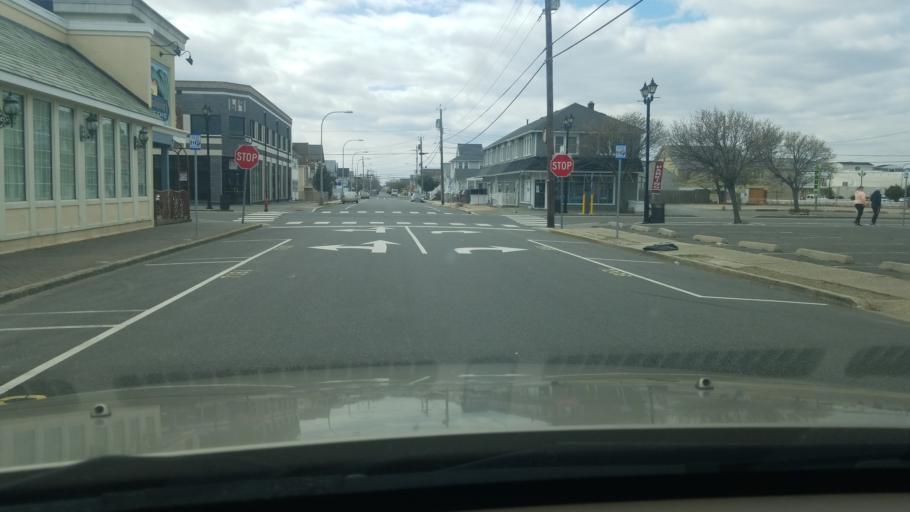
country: US
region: New Jersey
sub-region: Ocean County
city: Seaside Heights
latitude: 39.9419
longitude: -74.0732
